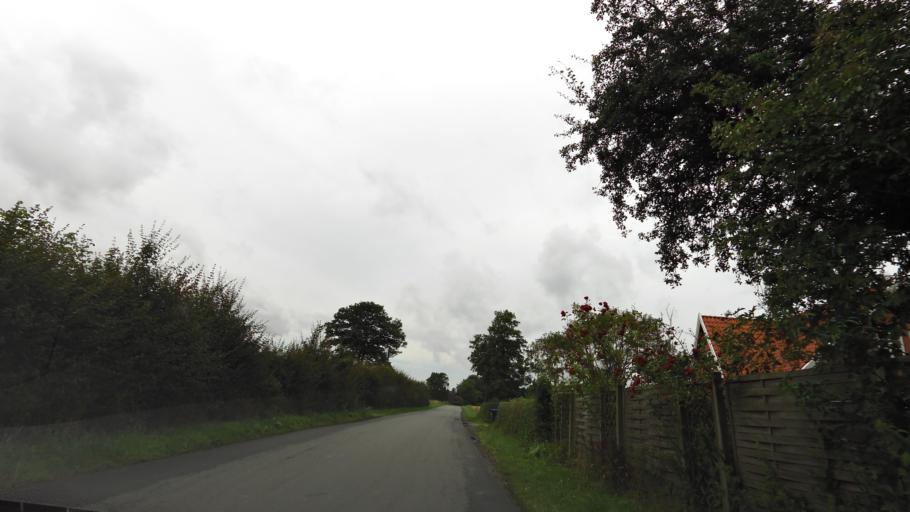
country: DK
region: South Denmark
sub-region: Nordfyns Kommune
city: Otterup
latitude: 55.5558
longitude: 10.4194
